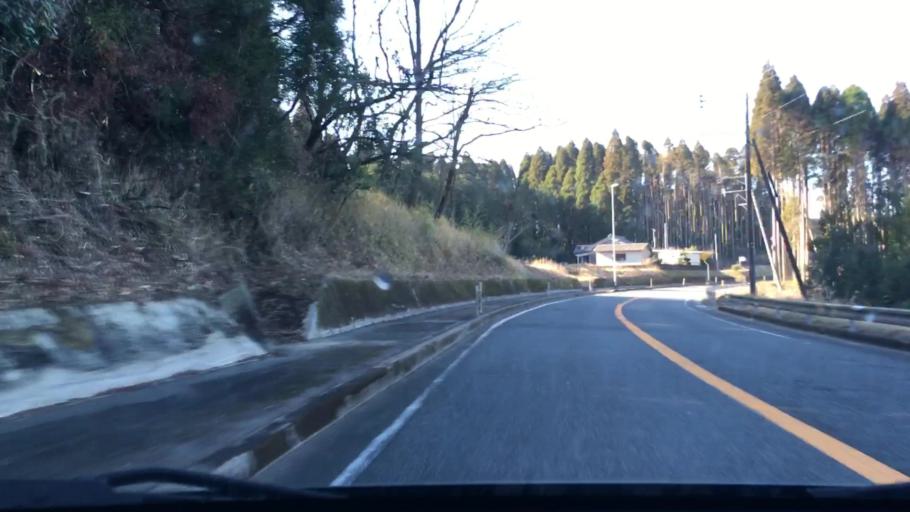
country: JP
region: Kagoshima
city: Sueyoshicho-ninokata
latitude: 31.6792
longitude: 130.9355
